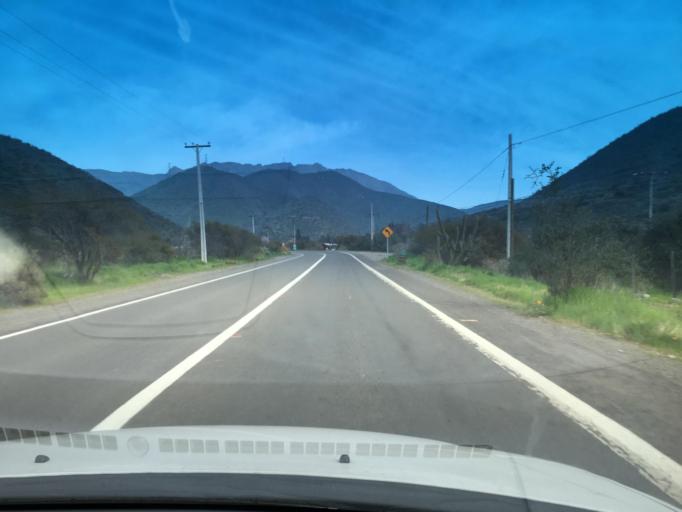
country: CL
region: Santiago Metropolitan
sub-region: Provincia de Chacabuco
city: Lampa
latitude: -33.0751
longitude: -70.9377
